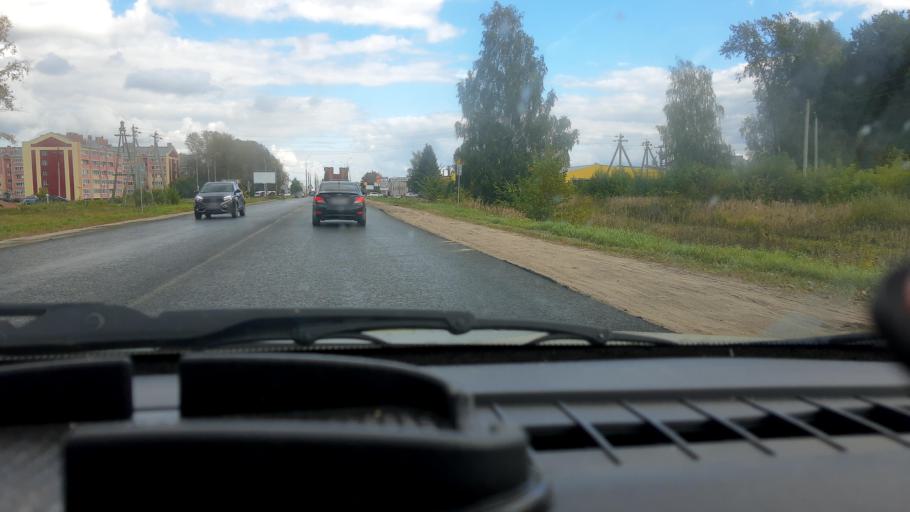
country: RU
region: Mariy-El
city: Medvedevo
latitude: 56.6378
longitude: 47.7661
